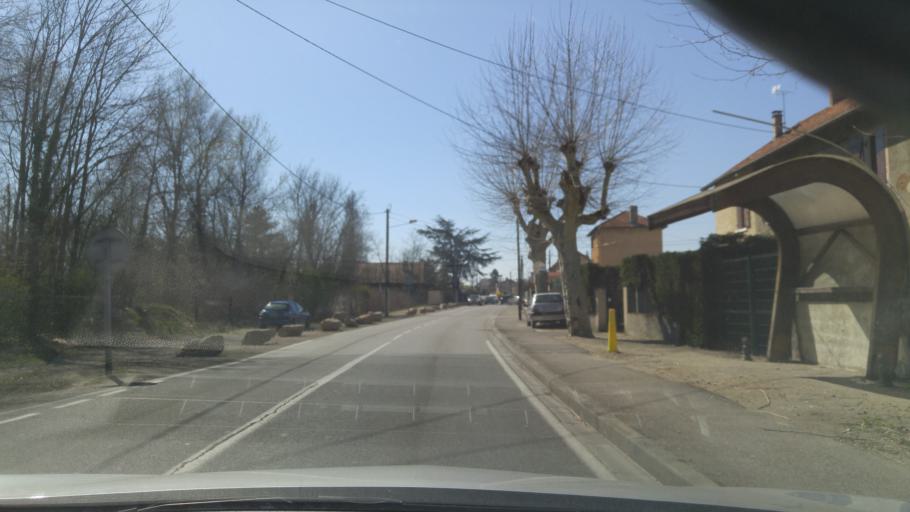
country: FR
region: Rhone-Alpes
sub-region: Departement de l'Isere
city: Tignieu-Jameyzieu
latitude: 45.7436
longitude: 5.1671
